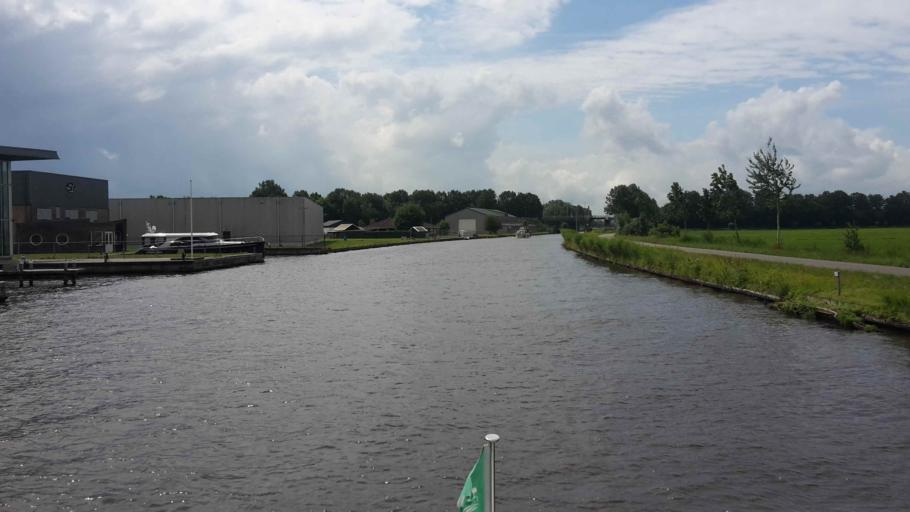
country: NL
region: Overijssel
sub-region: Gemeente Steenwijkerland
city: Tuk
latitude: 52.7768
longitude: 6.0877
